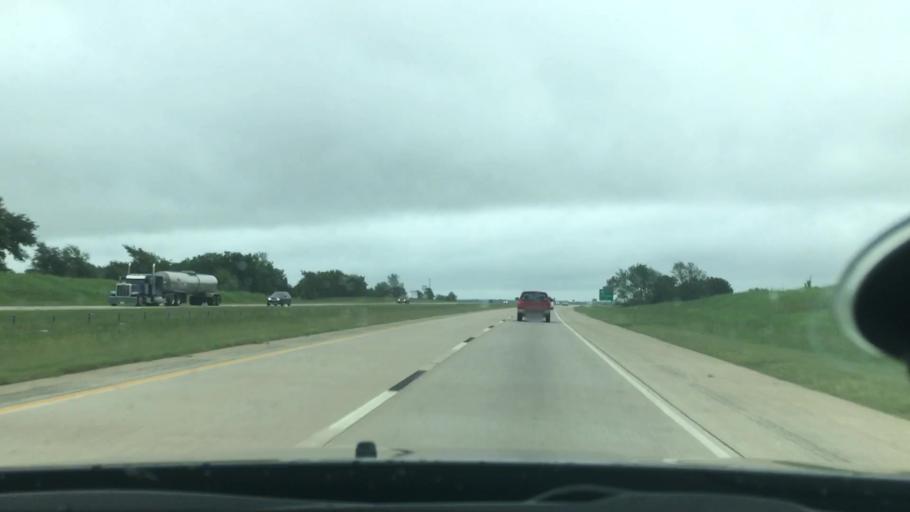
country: US
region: Oklahoma
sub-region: Okmulgee County
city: Wilson
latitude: 35.4310
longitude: -96.1319
